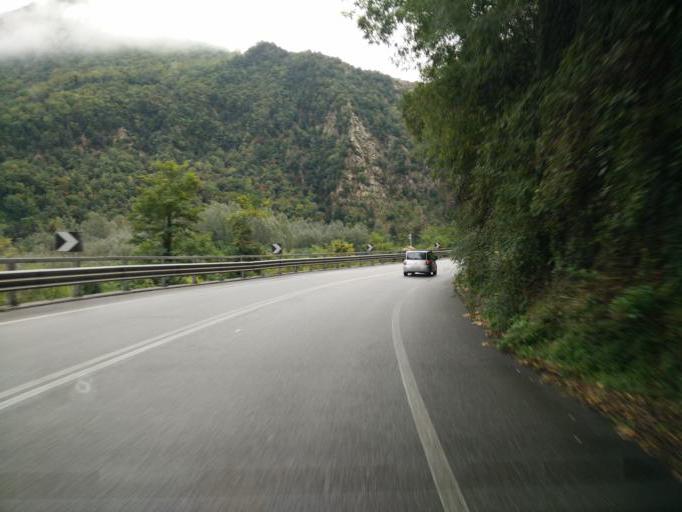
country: IT
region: Tuscany
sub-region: Provincia di Lucca
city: Valdottavo
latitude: 43.9341
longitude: 10.5069
